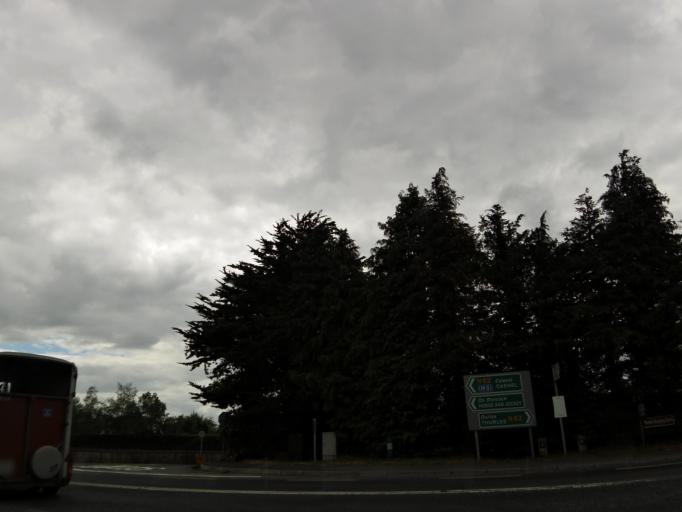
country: IE
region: Munster
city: Thurles
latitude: 52.6578
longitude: -7.8008
